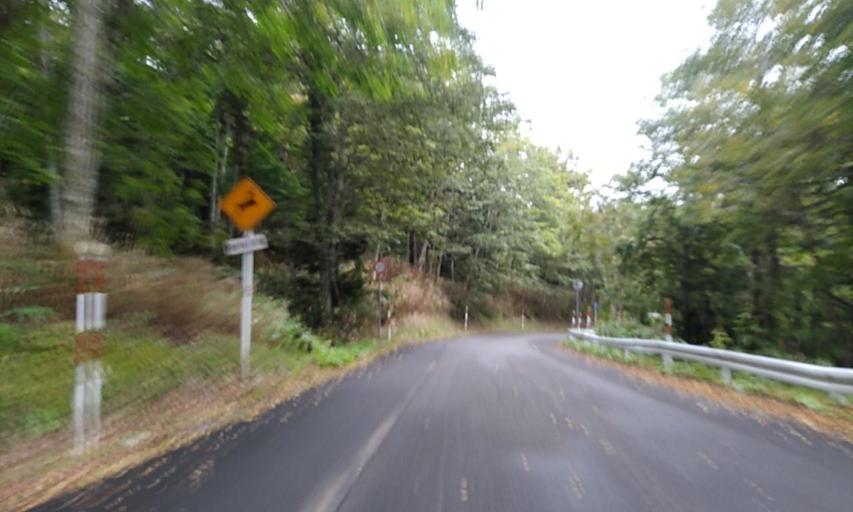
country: JP
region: Hokkaido
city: Bihoro
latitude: 43.5662
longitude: 144.1928
